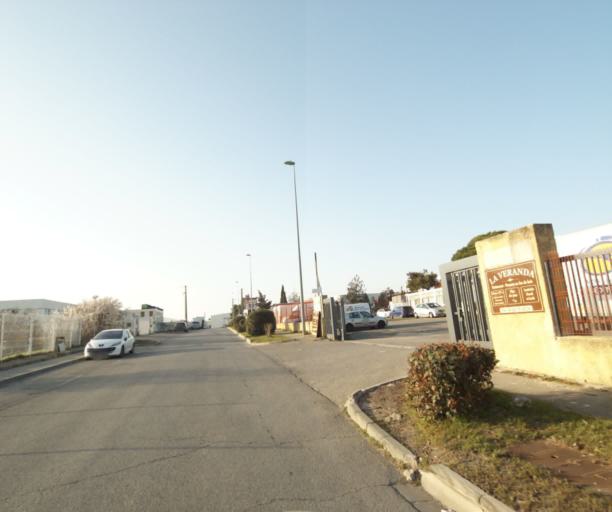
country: FR
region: Provence-Alpes-Cote d'Azur
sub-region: Departement des Bouches-du-Rhone
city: Saint-Victoret
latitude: 43.4261
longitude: 5.2393
